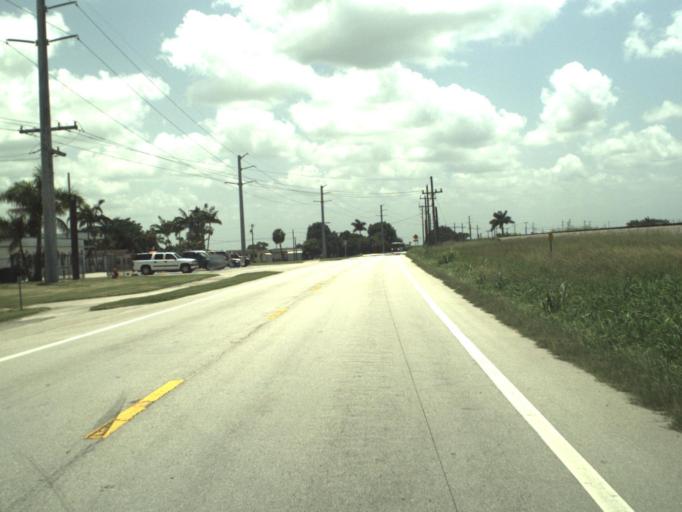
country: US
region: Florida
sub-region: Palm Beach County
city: Pahokee
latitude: 26.8334
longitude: -80.6445
